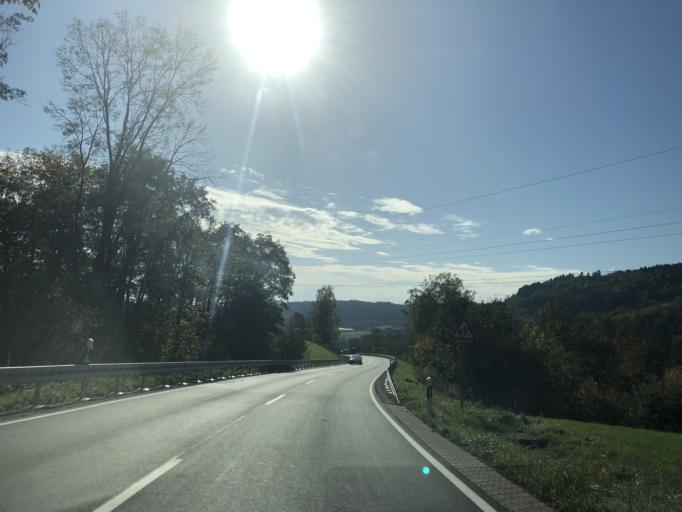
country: DE
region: Bavaria
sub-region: Lower Bavaria
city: Grafling
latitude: 48.8871
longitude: 12.9685
